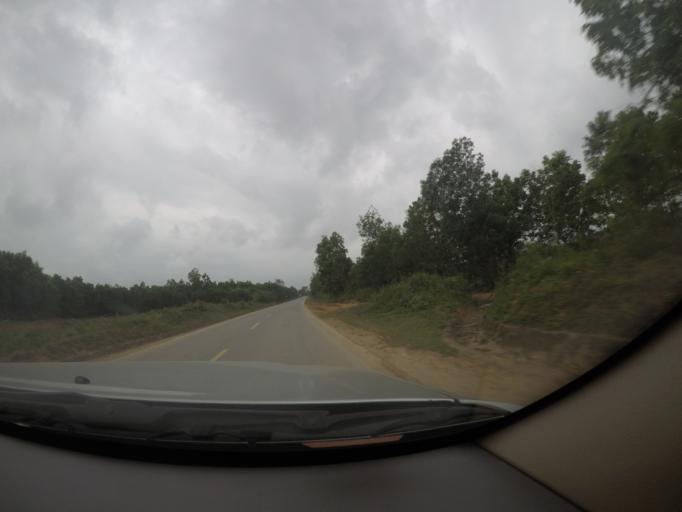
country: VN
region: Quang Tri
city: Cam Lo
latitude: 16.8454
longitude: 106.9990
